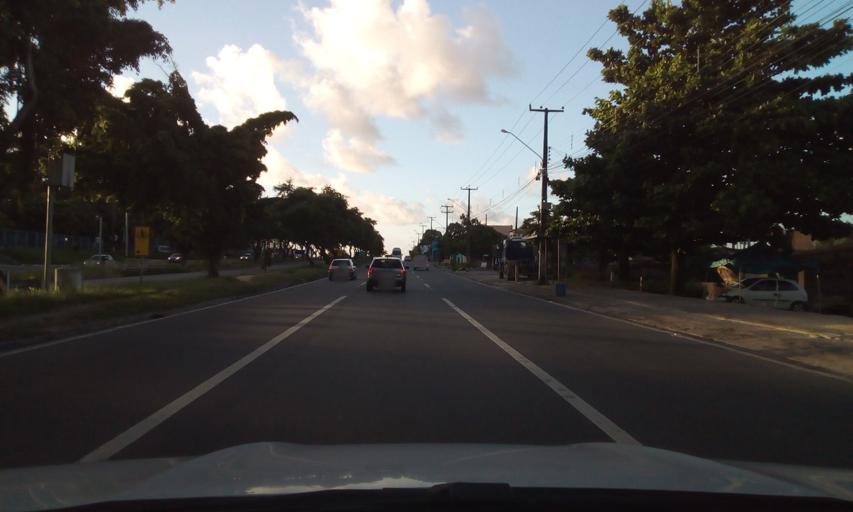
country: BR
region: Pernambuco
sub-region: Igarassu
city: Igarassu
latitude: -7.8621
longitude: -34.9076
